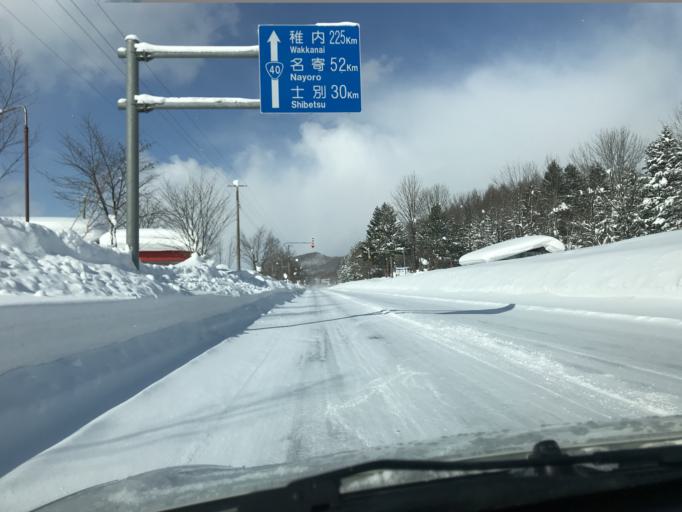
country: JP
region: Hokkaido
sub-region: Asahikawa-shi
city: Asahikawa
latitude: 43.9283
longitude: 142.4734
